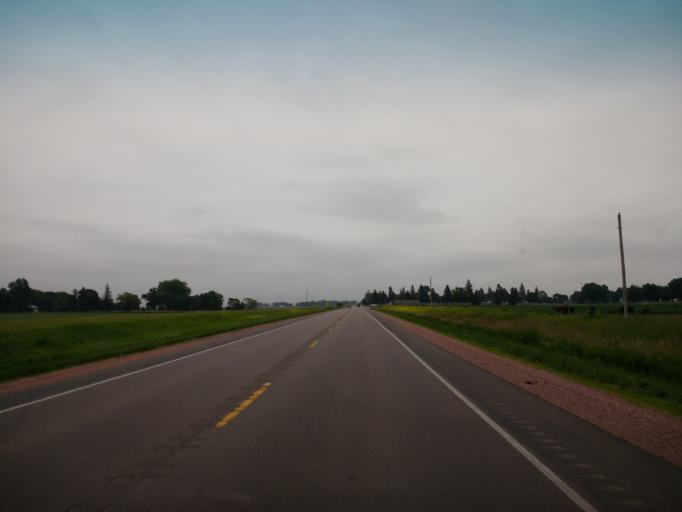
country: US
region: Iowa
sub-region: O'Brien County
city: Sanborn
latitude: 43.1861
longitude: -95.6878
